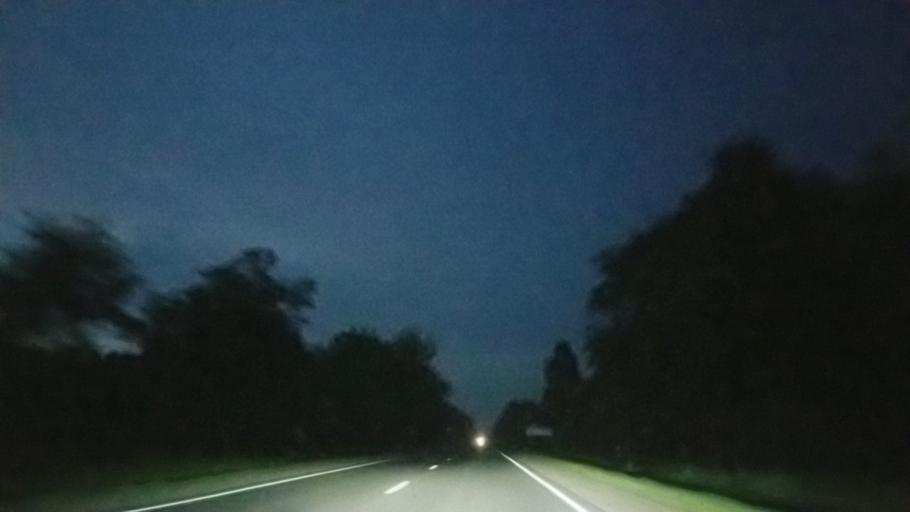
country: PL
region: Lublin Voivodeship
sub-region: Powiat bialski
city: Koden
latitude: 51.9624
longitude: 23.6833
